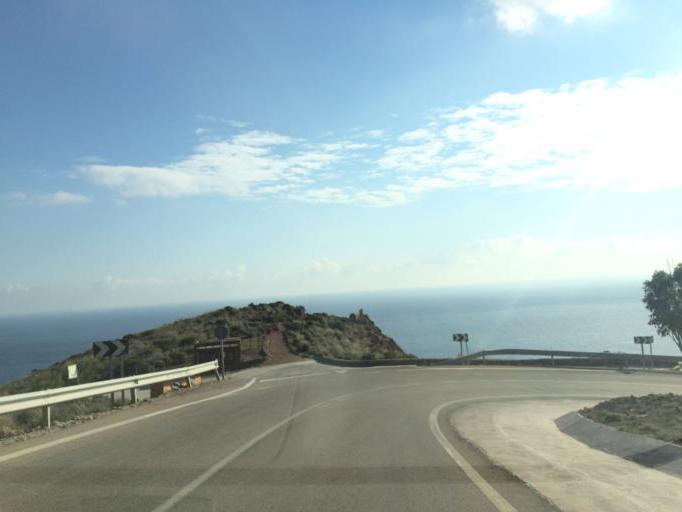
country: ES
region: Andalusia
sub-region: Provincia de Almeria
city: San Jose
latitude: 36.8283
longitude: -2.0398
